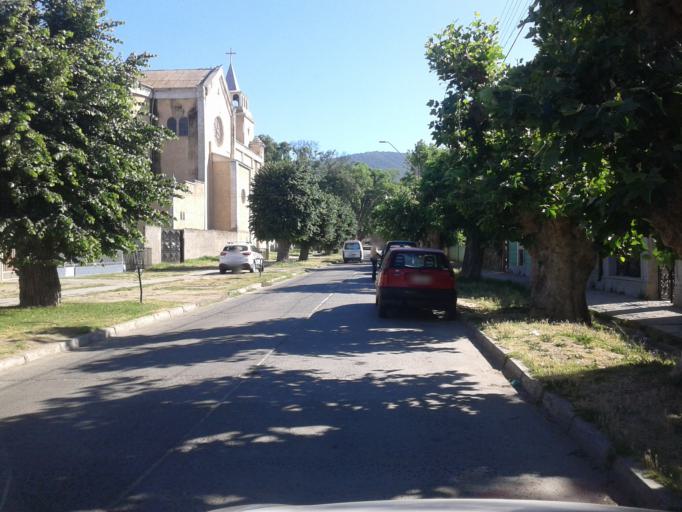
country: CL
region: Valparaiso
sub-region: Provincia de Marga Marga
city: Limache
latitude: -32.9885
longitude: -71.2743
